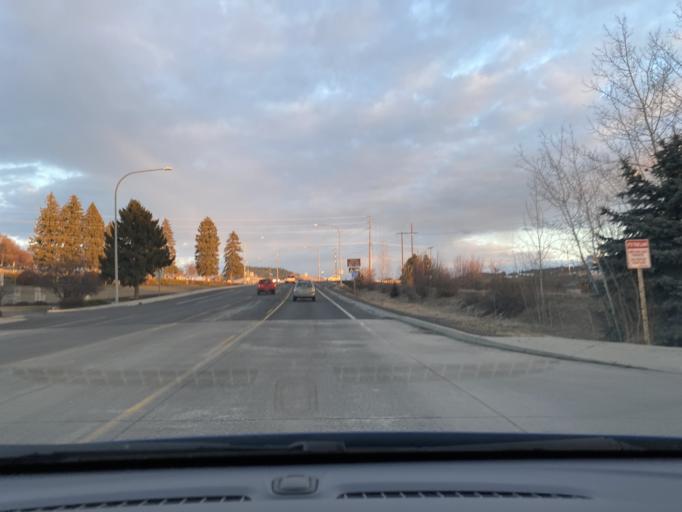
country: US
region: Idaho
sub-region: Latah County
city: Moscow
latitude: 46.7201
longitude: -116.9824
